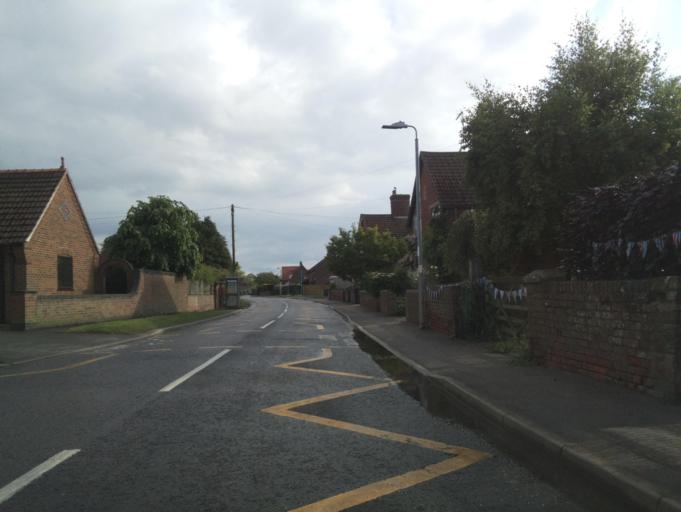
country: GB
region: England
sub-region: Lincolnshire
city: Great Gonerby
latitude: 52.9829
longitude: -0.6737
